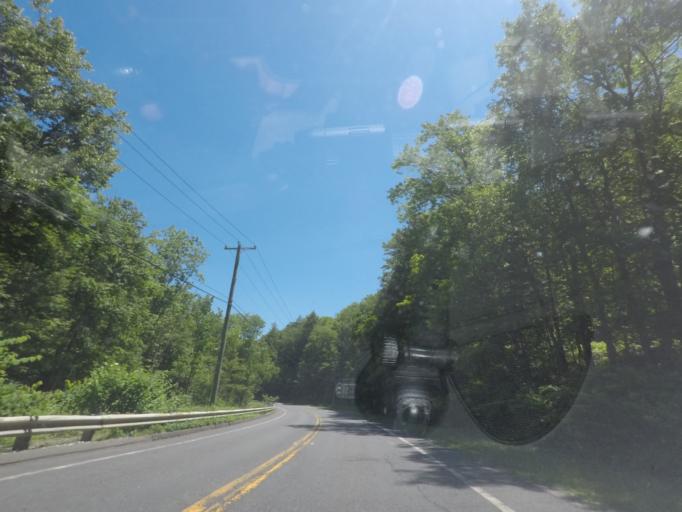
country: US
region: Massachusetts
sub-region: Berkshire County
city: Becket
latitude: 42.2693
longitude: -73.0178
